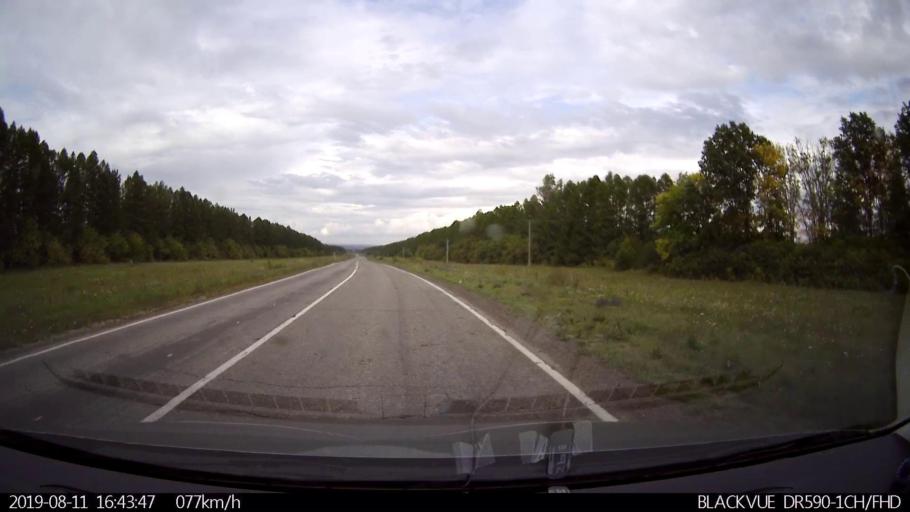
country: RU
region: Ulyanovsk
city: Mayna
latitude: 54.1719
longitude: 47.6754
